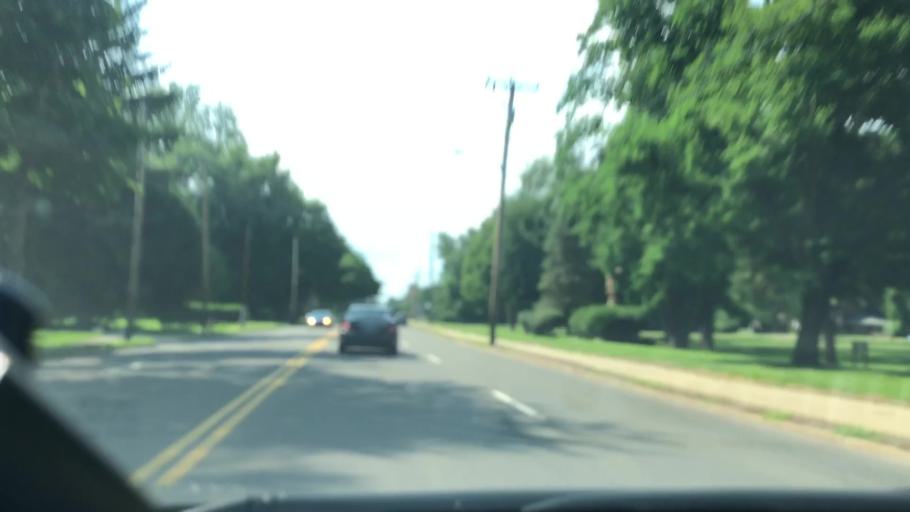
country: US
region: Ohio
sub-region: Summit County
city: Fairlawn
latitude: 41.1163
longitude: -81.5847
